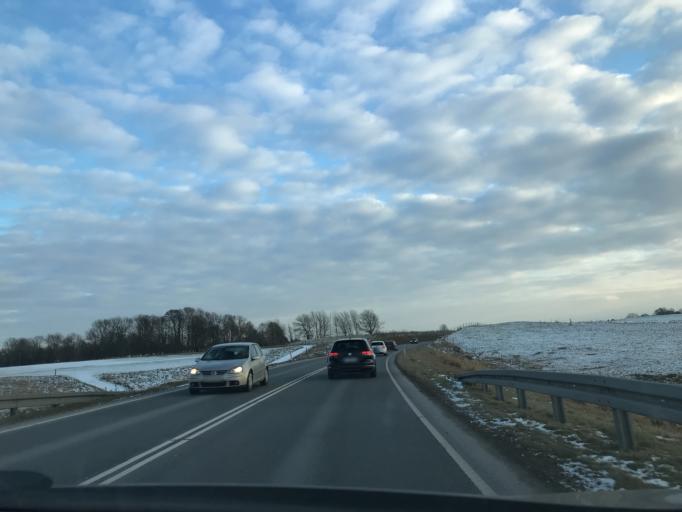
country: DK
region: Capital Region
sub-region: Egedal Kommune
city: Smorumnedre
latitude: 55.7265
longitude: 12.3129
